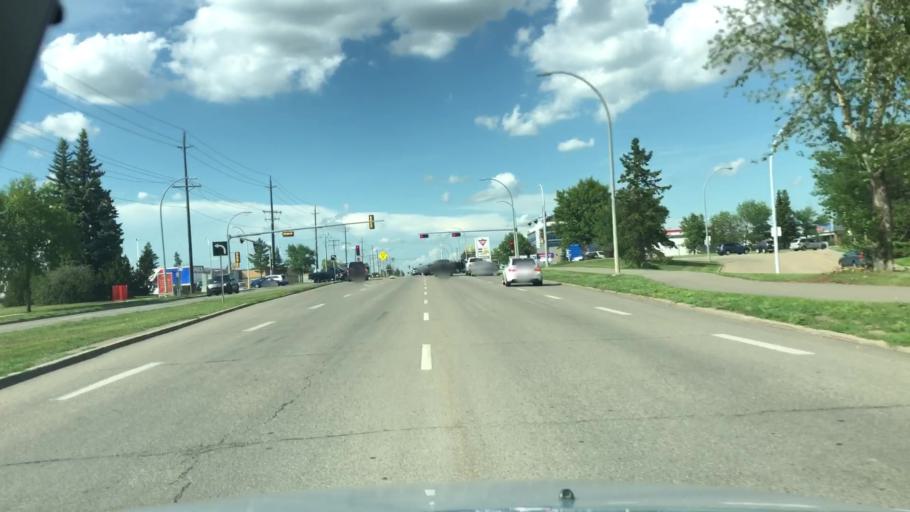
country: CA
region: Alberta
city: Edmonton
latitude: 53.5363
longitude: -113.4185
